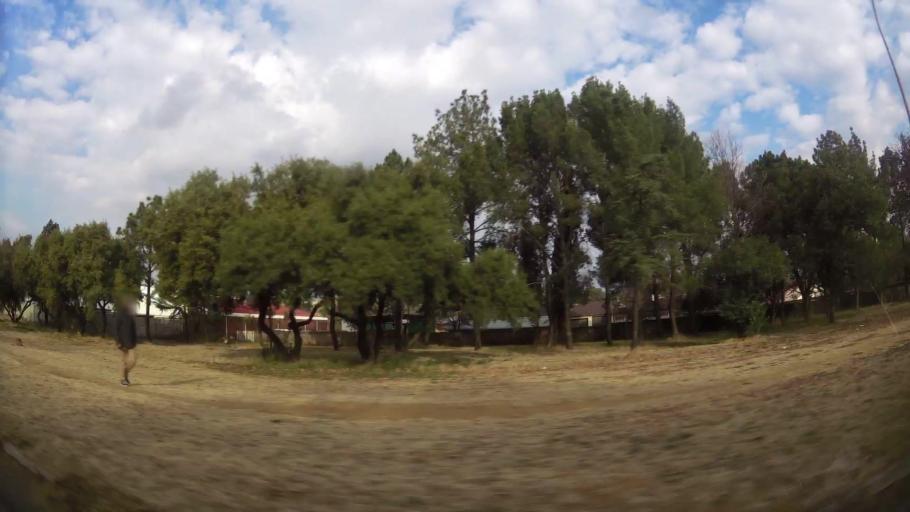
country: ZA
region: Orange Free State
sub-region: Fezile Dabi District Municipality
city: Sasolburg
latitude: -26.8254
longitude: 27.8296
